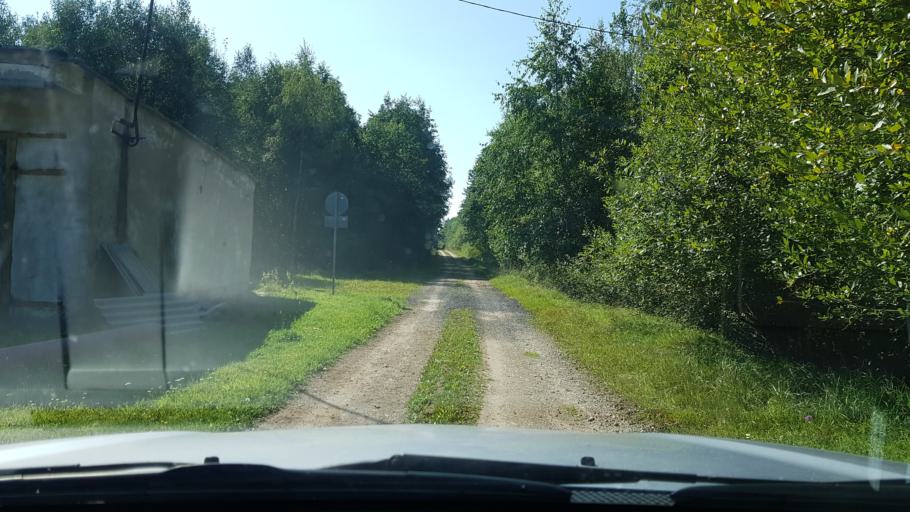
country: EE
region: Ida-Virumaa
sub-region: Sillamaee linn
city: Sillamae
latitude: 59.3458
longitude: 27.7367
